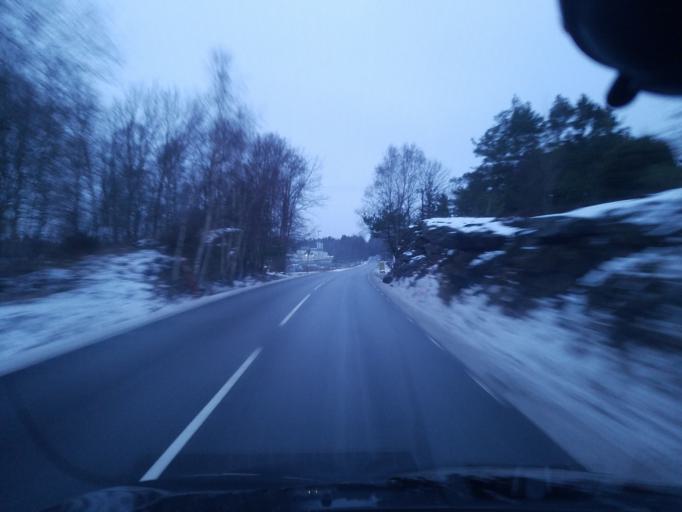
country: SE
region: Vaestra Goetaland
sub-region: Lysekils Kommun
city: Lysekil
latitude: 58.2947
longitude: 11.4769
